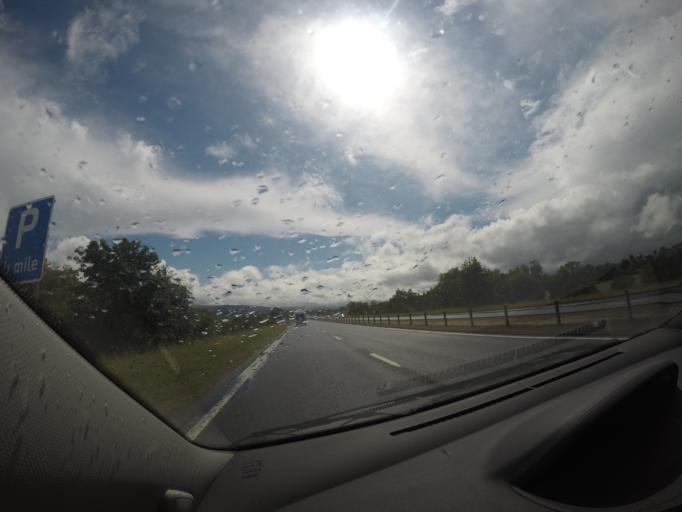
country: GB
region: Scotland
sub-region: Perth and Kinross
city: Auchterarder
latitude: 56.3142
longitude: -3.6577
